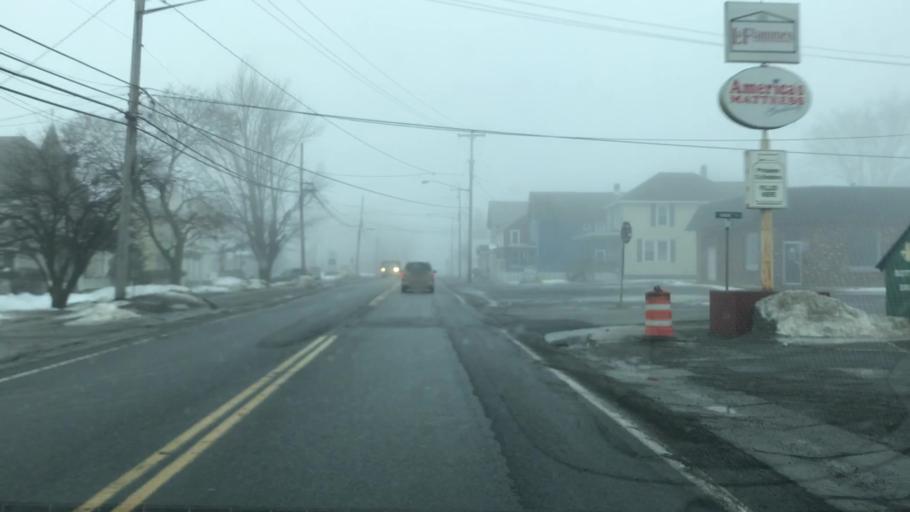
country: US
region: New York
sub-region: Washington County
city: Whitehall
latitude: 43.5465
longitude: -73.4064
